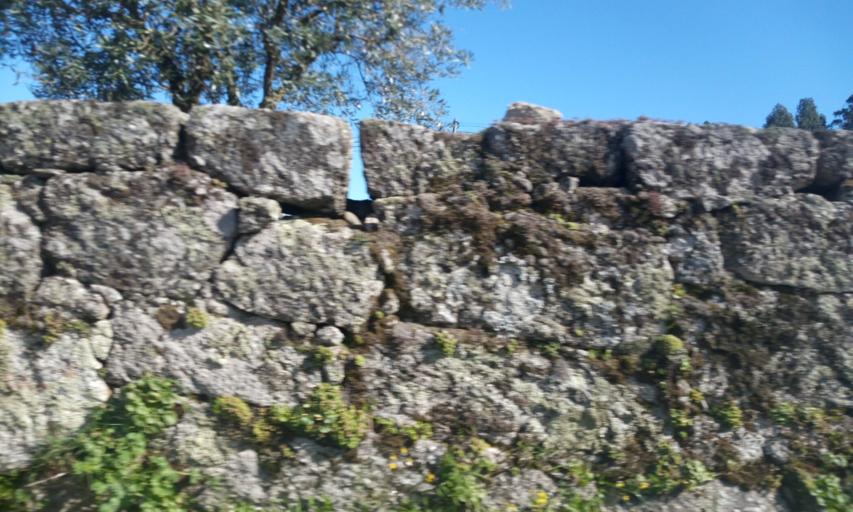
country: PT
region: Guarda
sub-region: Manteigas
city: Manteigas
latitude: 40.5087
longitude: -7.6091
